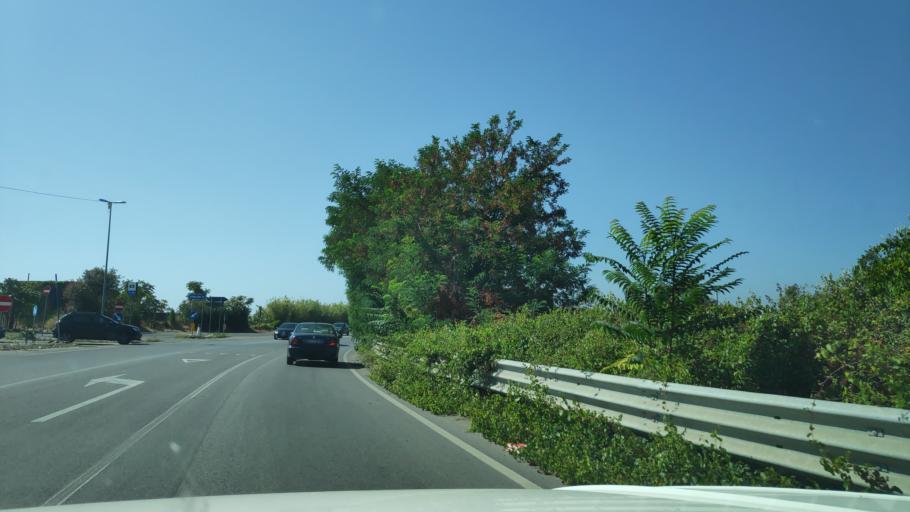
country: IT
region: Calabria
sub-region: Provincia di Reggio Calabria
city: Bovalino
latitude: 38.1388
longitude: 16.1656
